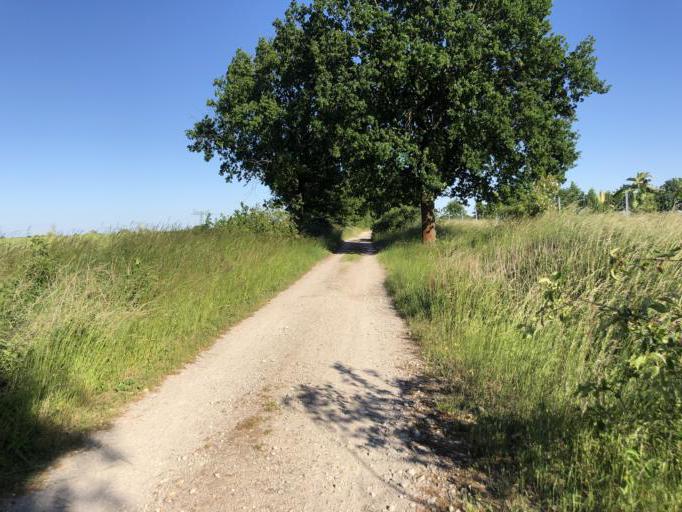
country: DE
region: Brandenburg
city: Schonefeld
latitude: 52.3473
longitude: 13.4966
